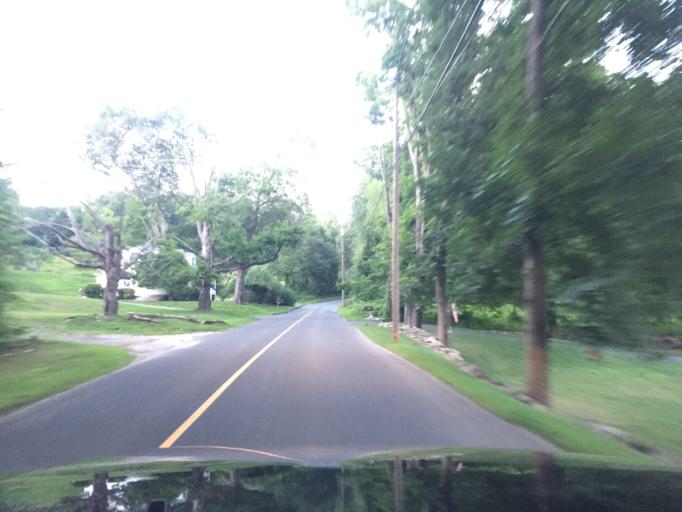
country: US
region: Connecticut
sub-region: Fairfield County
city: Bethel
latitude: 41.4096
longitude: -73.3749
